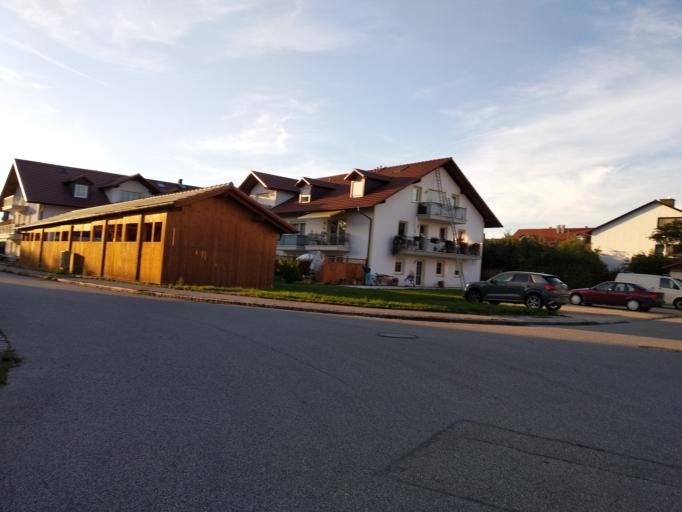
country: DE
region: Bavaria
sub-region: Upper Bavaria
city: Steinhoring
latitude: 48.0880
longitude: 12.0337
